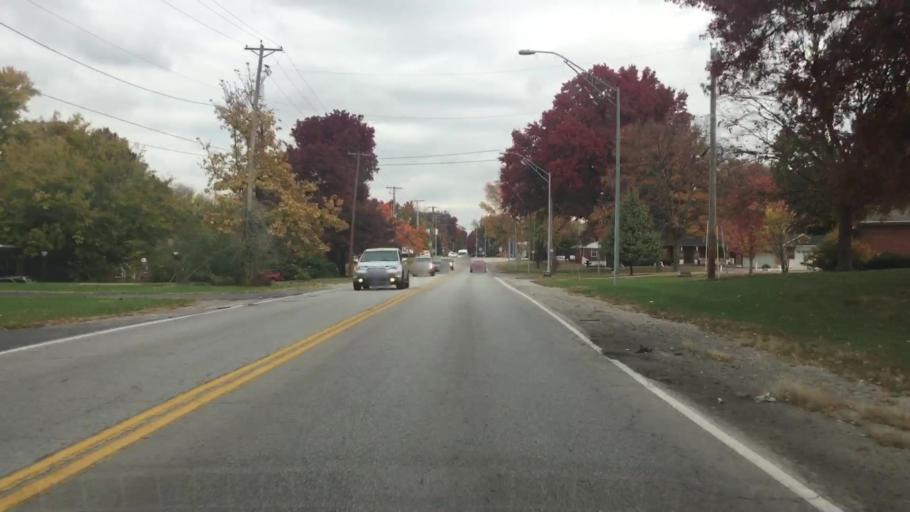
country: US
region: Missouri
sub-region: Jackson County
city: Raytown
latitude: 39.0340
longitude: -94.4390
